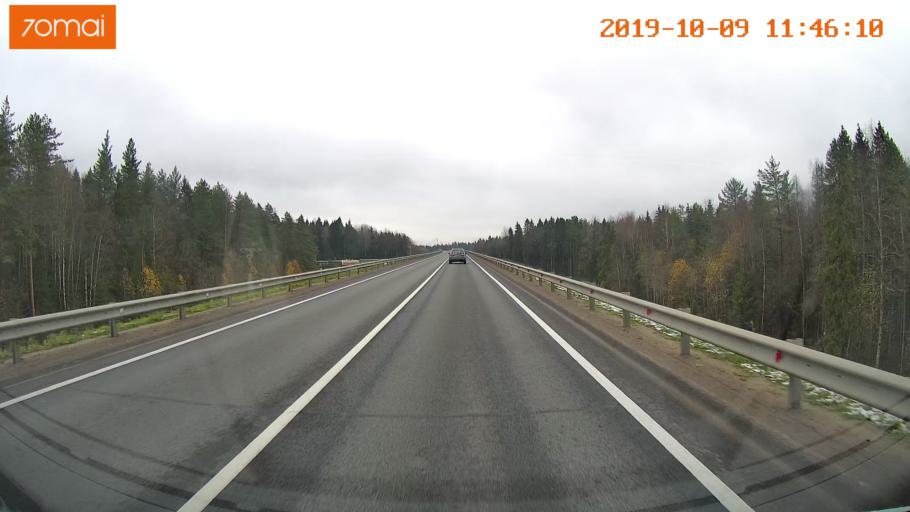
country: RU
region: Vologda
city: Gryazovets
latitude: 58.8579
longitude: 40.1999
